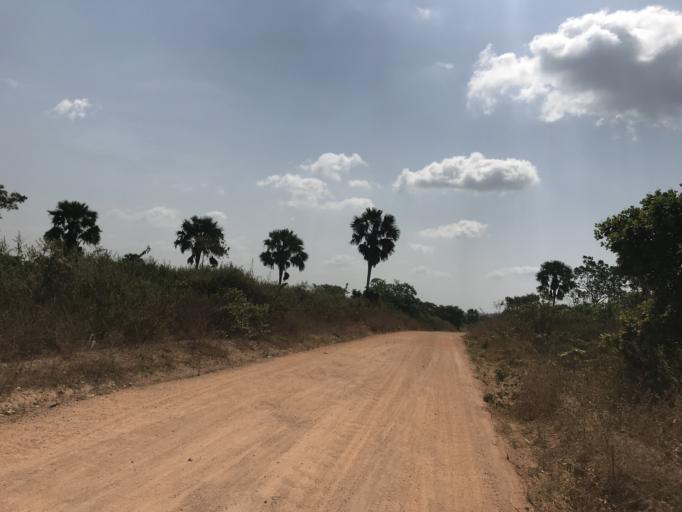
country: NG
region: Osun
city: Ifon
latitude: 7.9369
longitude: 4.4854
